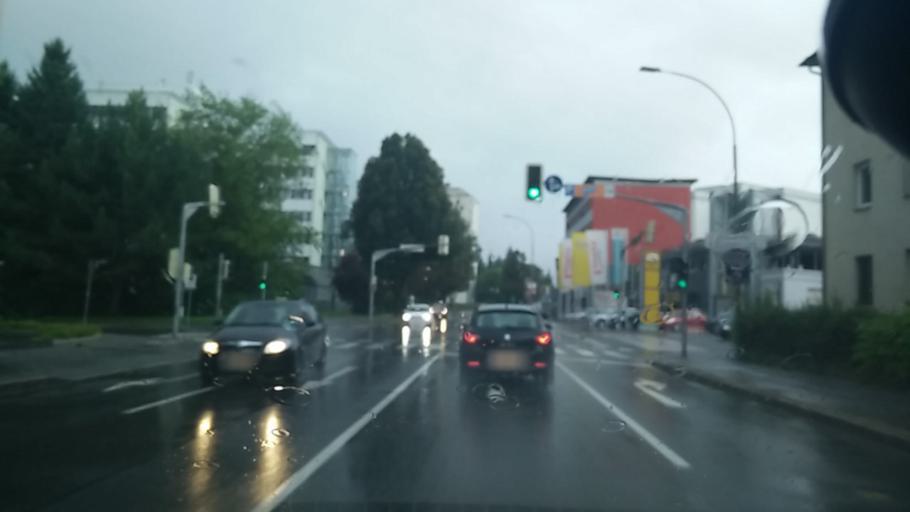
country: AT
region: Carinthia
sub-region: Villach Stadt
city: Villach
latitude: 46.6081
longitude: 13.8501
